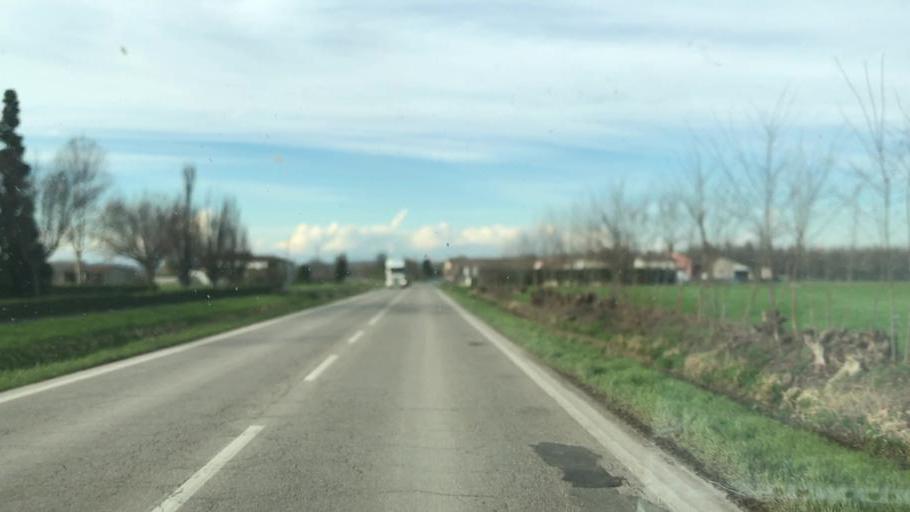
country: IT
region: Lombardy
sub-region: Provincia di Mantova
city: Cerlongo
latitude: 45.2849
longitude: 10.6574
